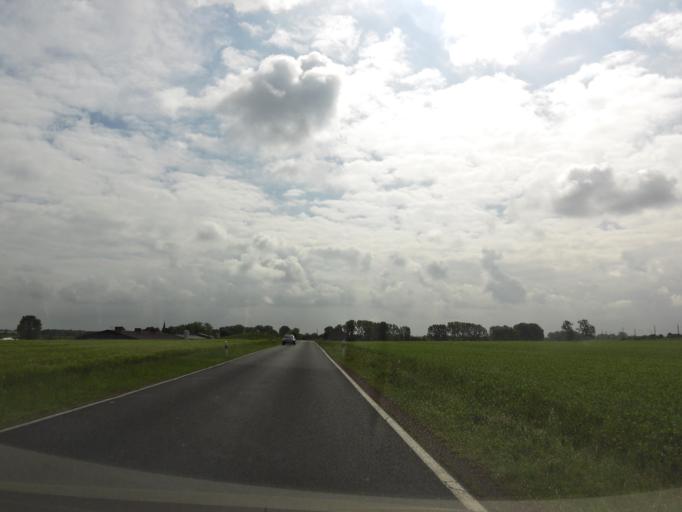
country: DE
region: Thuringia
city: Grabsleben
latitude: 50.9227
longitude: 10.8243
